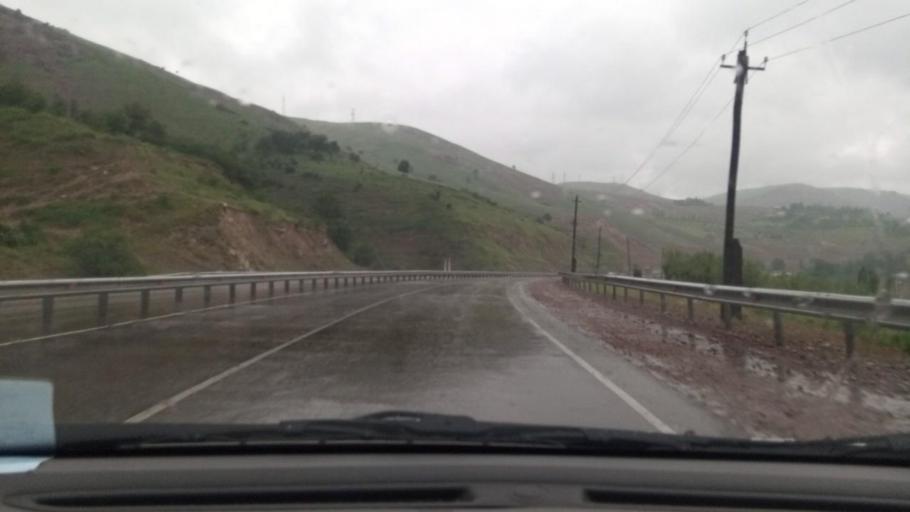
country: UZ
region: Toshkent
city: Angren
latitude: 41.0916
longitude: 70.3197
